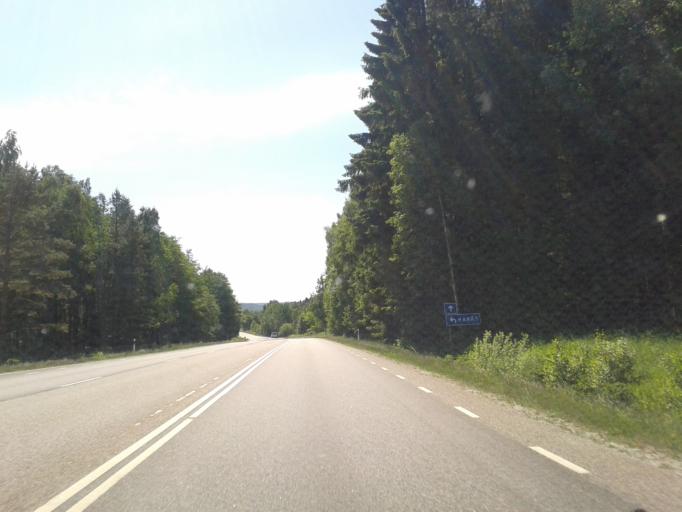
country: SE
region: Vaestra Goetaland
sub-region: Stenungsunds Kommun
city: Stora Hoga
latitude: 58.0502
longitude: 11.9011
